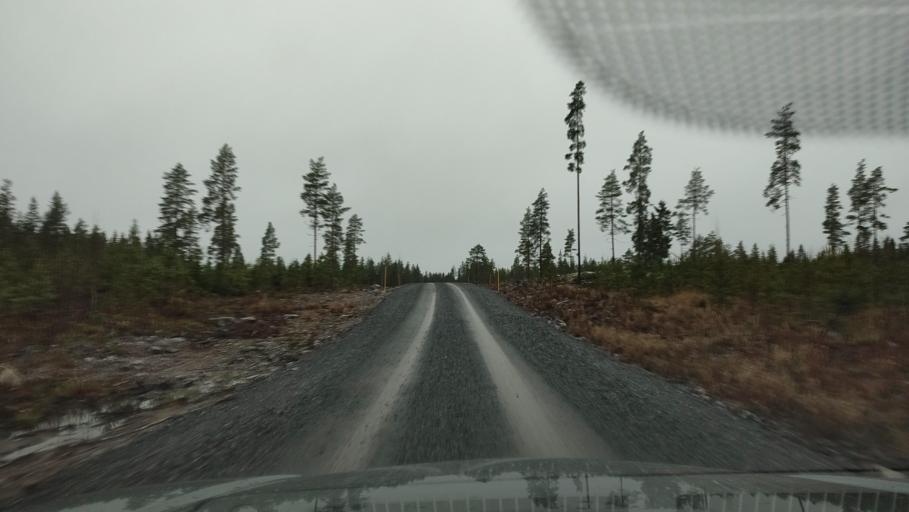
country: FI
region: Southern Ostrobothnia
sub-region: Suupohja
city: Karijoki
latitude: 62.1590
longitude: 21.5965
